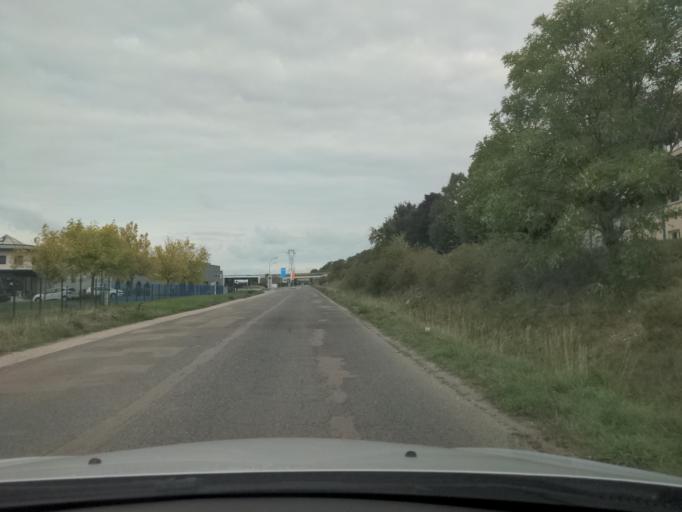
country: FR
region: Bourgogne
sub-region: Departement de la Cote-d'Or
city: Ahuy
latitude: 47.3558
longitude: 5.0404
